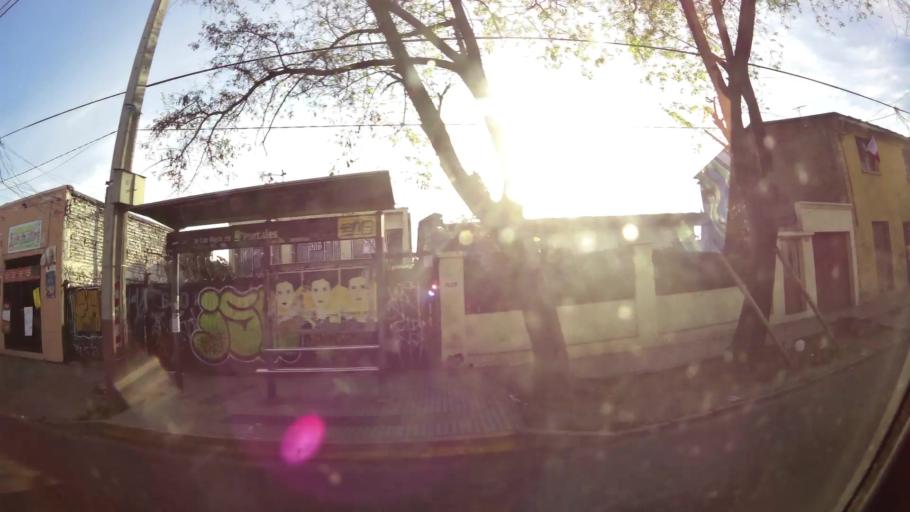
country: CL
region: Santiago Metropolitan
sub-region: Provincia de Santiago
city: Lo Prado
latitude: -33.4457
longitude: -70.7074
